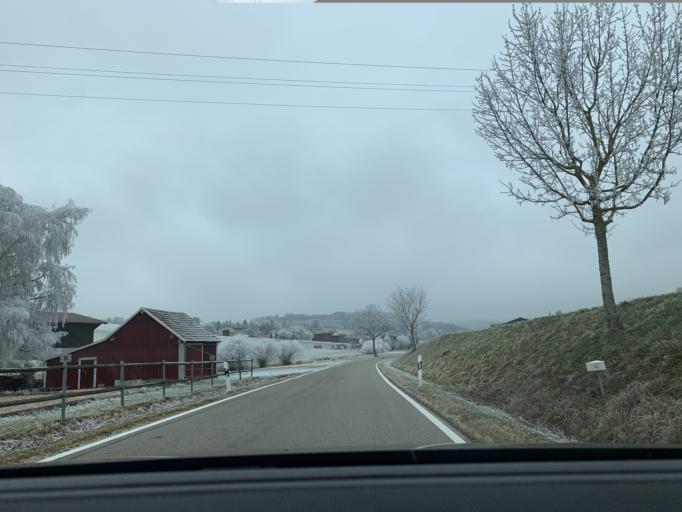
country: DE
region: Baden-Wuerttemberg
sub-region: Freiburg Region
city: Tengen
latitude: 47.8615
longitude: 8.6769
